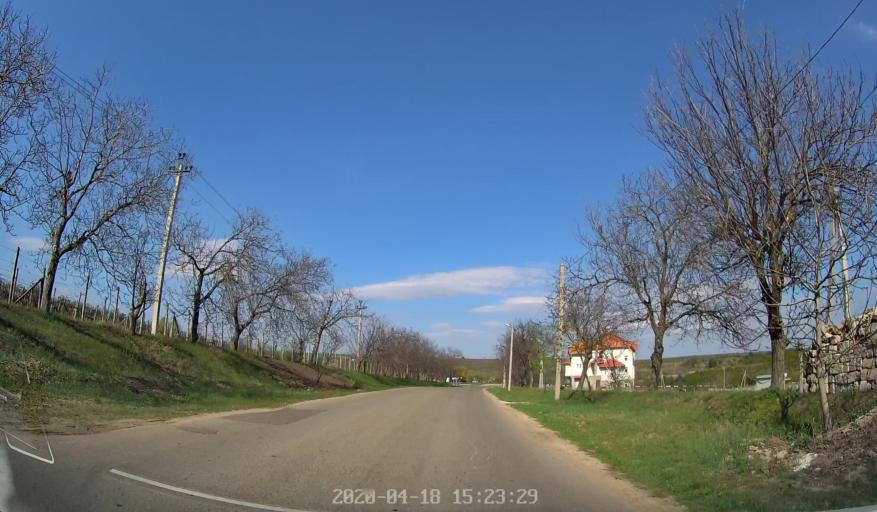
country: MD
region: Chisinau
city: Vadul lui Voda
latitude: 47.0690
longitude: 29.0160
